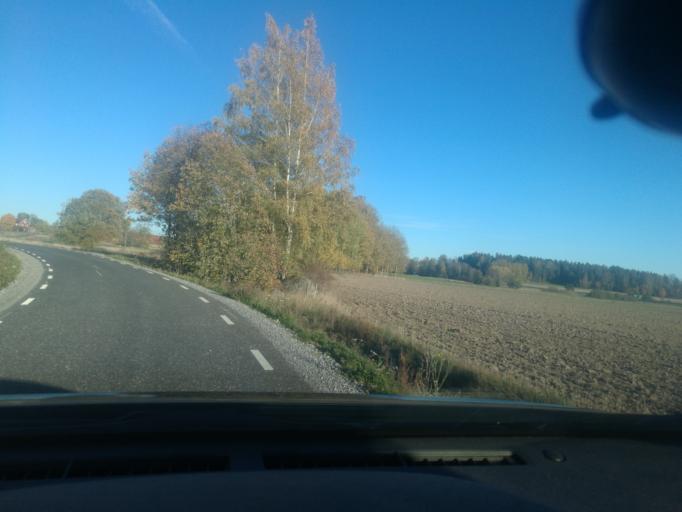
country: SE
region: Vaestmanland
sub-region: Kopings Kommun
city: Koping
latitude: 59.5676
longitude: 16.0703
